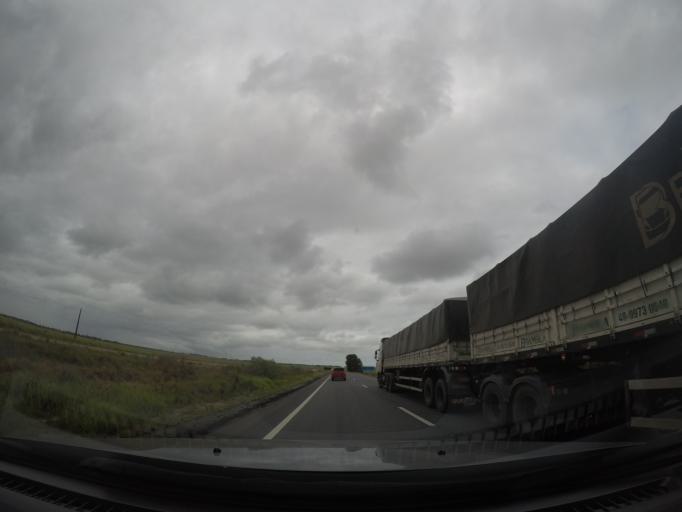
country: BR
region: Alagoas
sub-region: Pilar
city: Pilar
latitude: -9.6727
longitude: -36.0311
